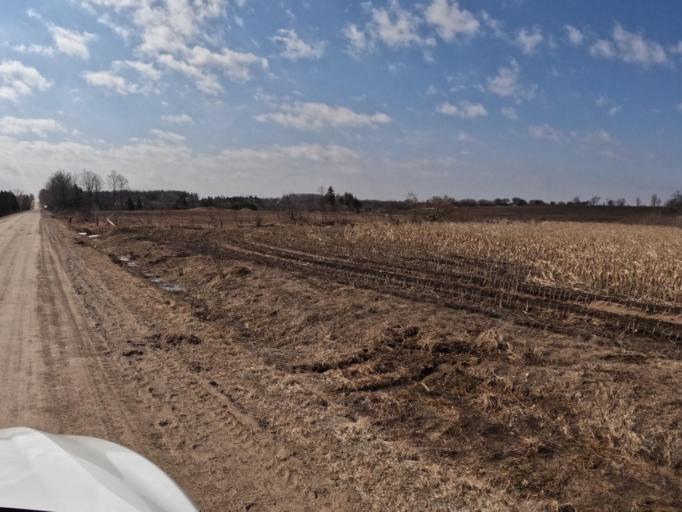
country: CA
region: Ontario
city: Orangeville
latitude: 43.9047
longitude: -80.2518
